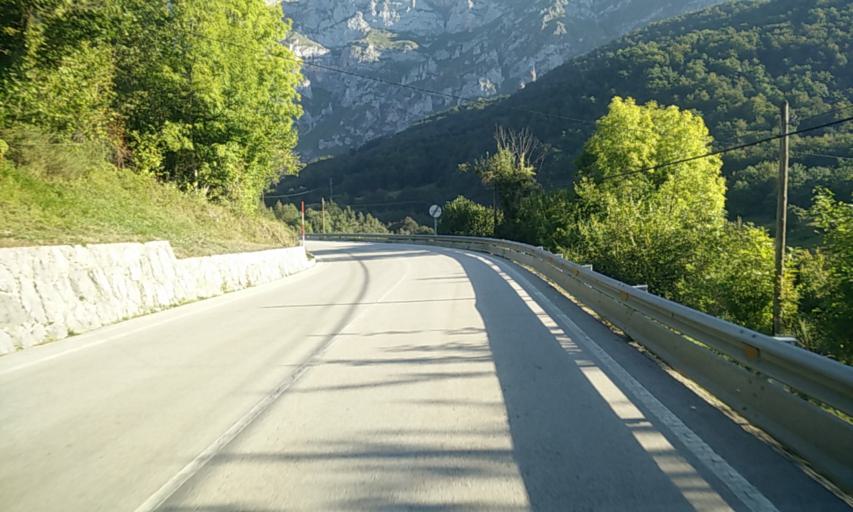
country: ES
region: Castille and Leon
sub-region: Provincia de Leon
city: Posada de Valdeon
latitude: 43.1357
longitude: -4.8107
